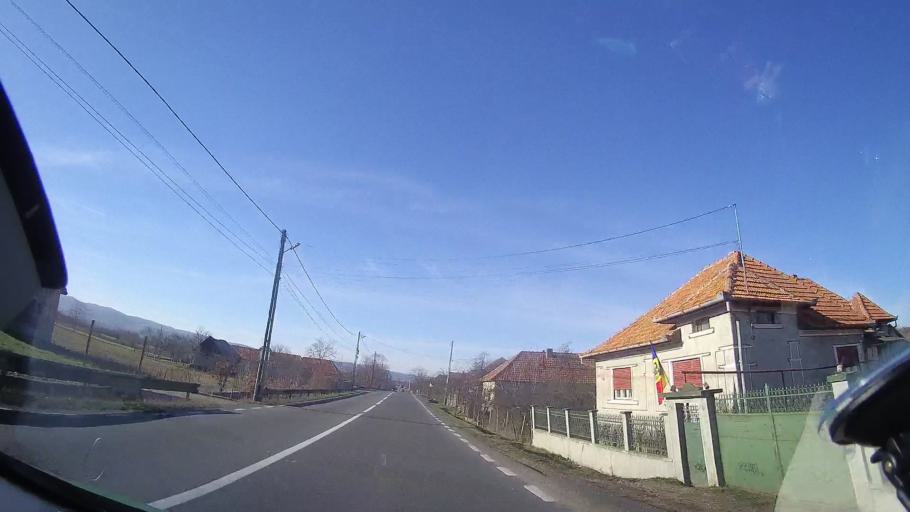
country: RO
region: Bihor
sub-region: Comuna Vadu Crisului
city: Vadu Crisului
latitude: 47.0016
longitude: 22.5427
